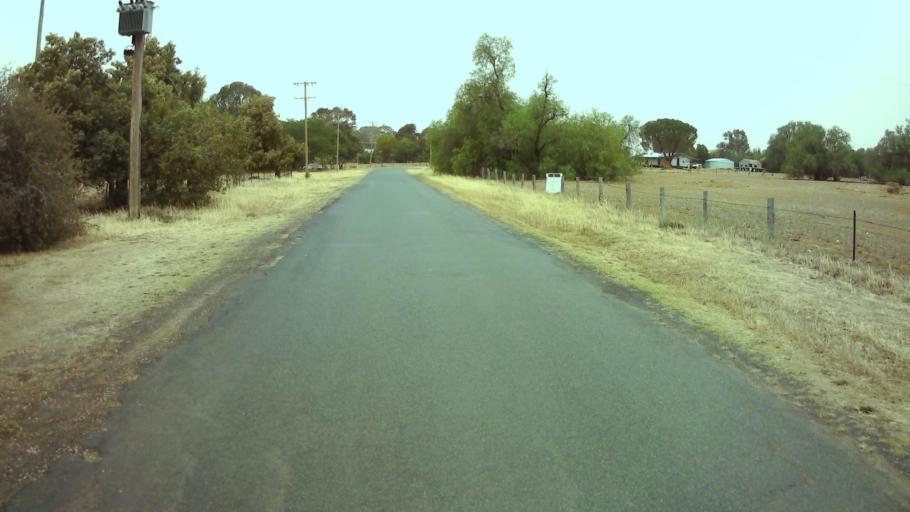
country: AU
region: New South Wales
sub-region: Weddin
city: Grenfell
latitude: -33.8998
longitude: 148.1678
